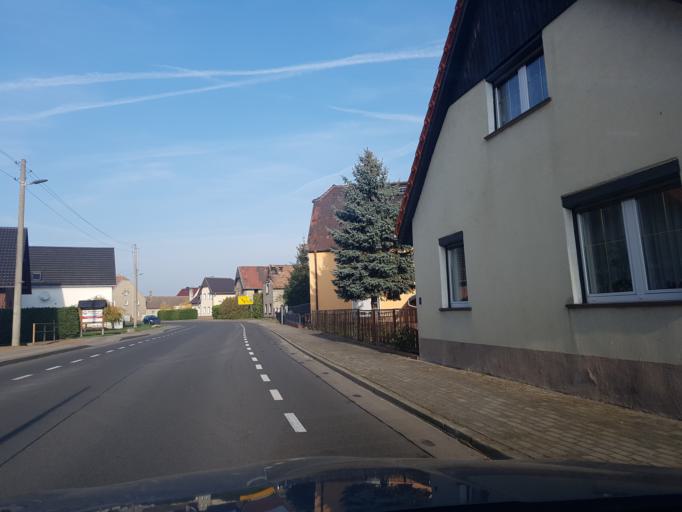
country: DE
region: Brandenburg
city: Falkenberg
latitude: 51.5421
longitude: 13.2807
